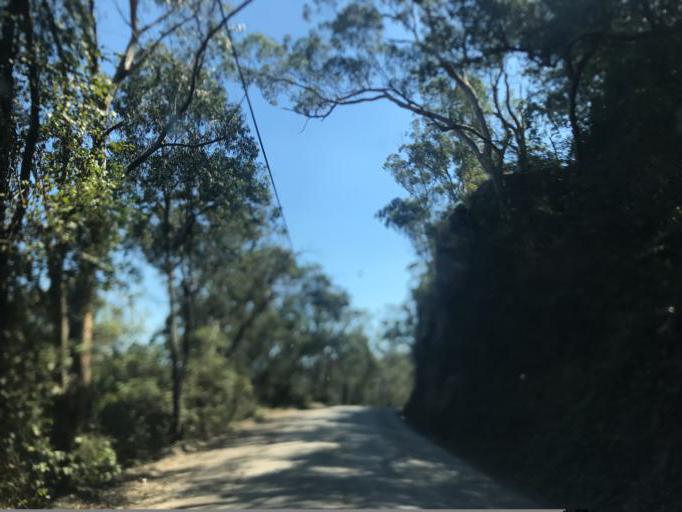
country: AU
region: New South Wales
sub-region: Hawkesbury
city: Pitt Town
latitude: -33.4359
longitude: 150.8942
